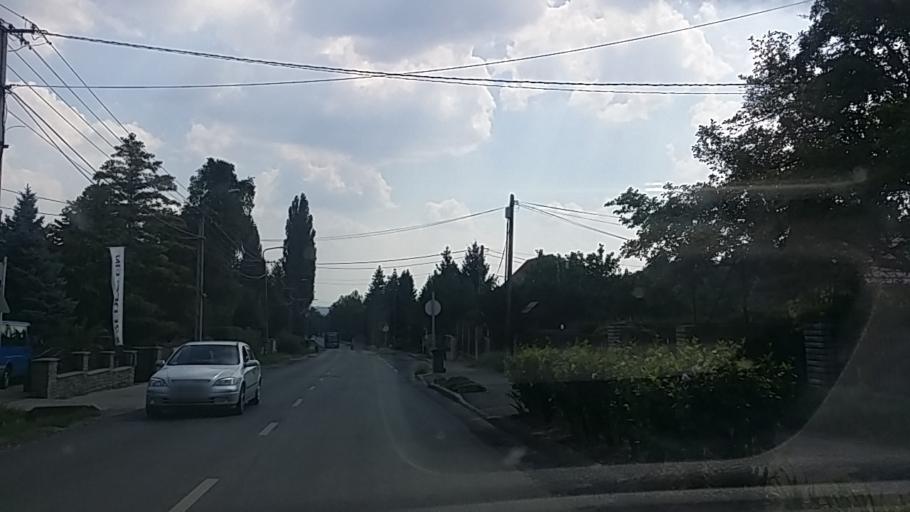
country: HU
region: Baranya
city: Pecs
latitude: 46.0761
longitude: 18.1869
